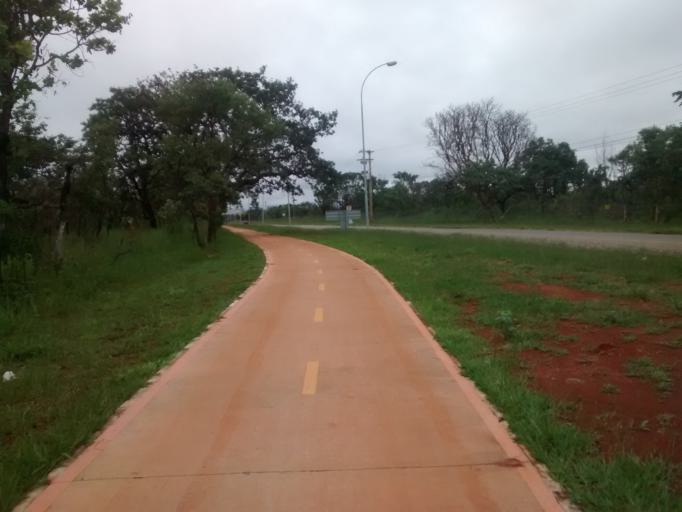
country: BR
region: Federal District
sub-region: Brasilia
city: Brasilia
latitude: -15.8066
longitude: -47.8393
